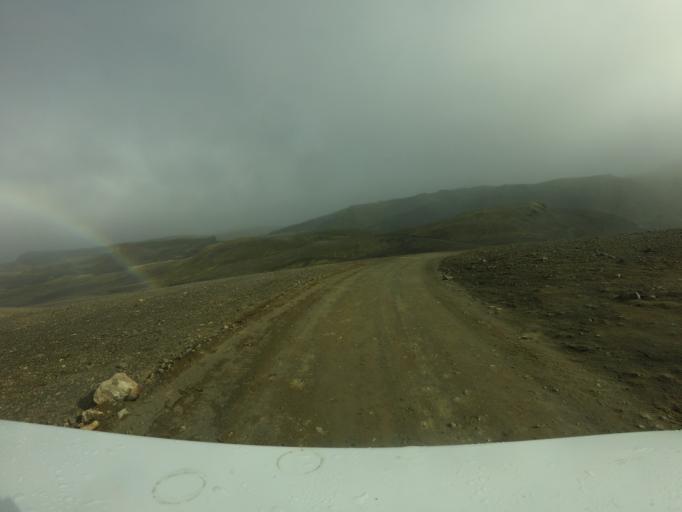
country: IS
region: South
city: Vestmannaeyjar
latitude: 63.9804
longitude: -18.8930
